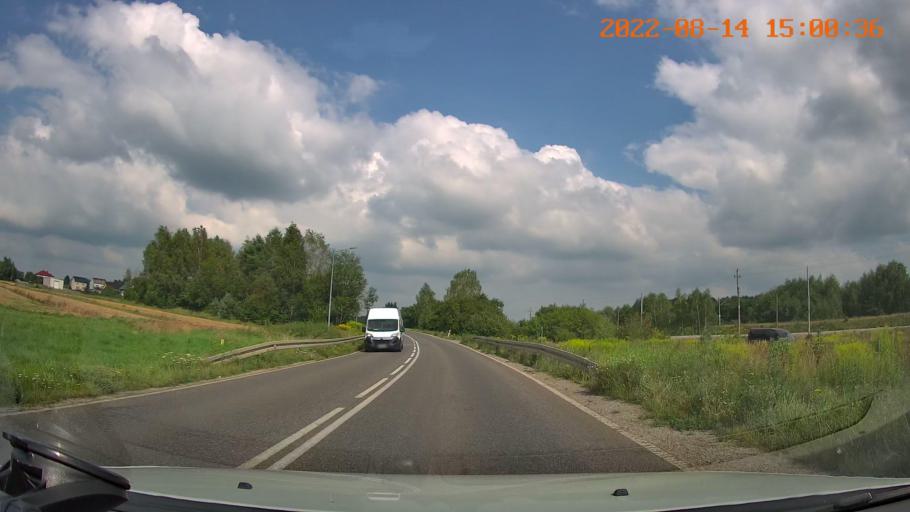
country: PL
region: Swietokrzyskie
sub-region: Powiat kielecki
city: Piekoszow
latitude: 50.8809
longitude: 20.4973
